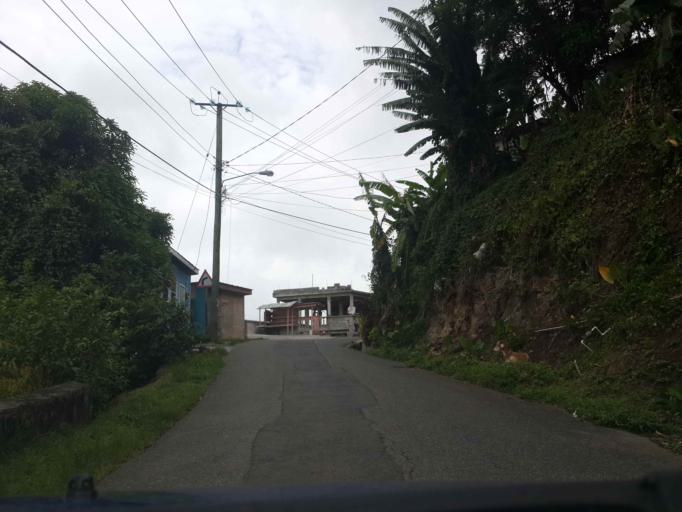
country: LC
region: Castries Quarter
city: Castries
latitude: 13.9954
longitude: -60.9820
